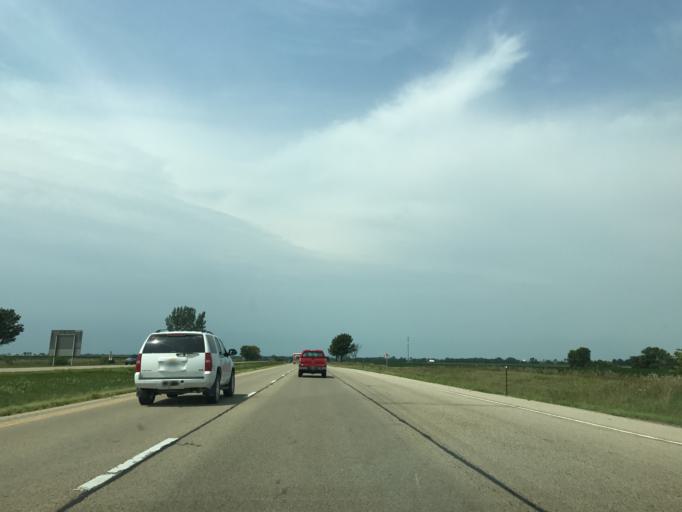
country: US
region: Illinois
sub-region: Bureau County
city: Ladd
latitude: 41.3686
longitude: -89.2235
